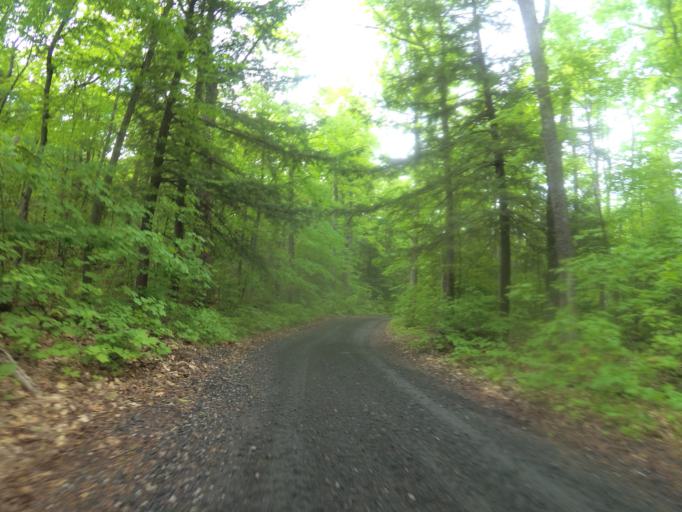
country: CA
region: Ontario
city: Renfrew
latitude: 45.1121
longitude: -76.8245
